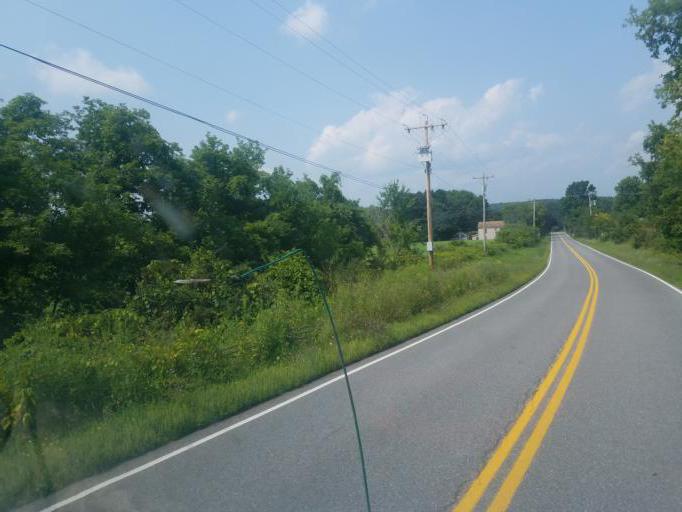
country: US
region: New York
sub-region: Montgomery County
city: Tribes Hill
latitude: 42.9264
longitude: -74.3169
